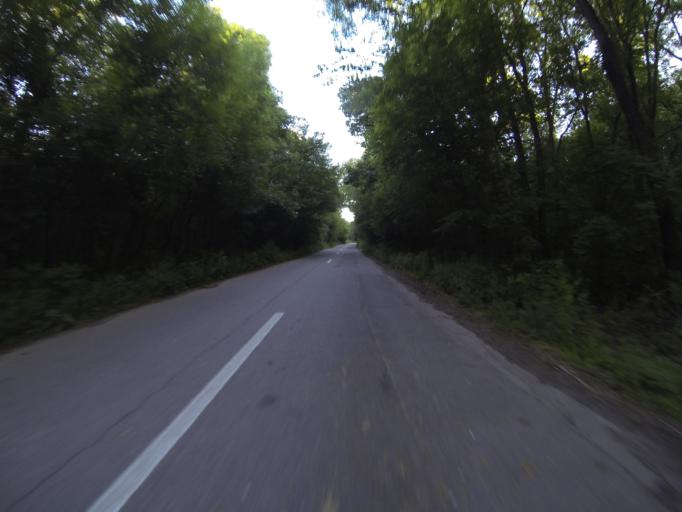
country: RO
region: Dolj
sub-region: Comuna Tuglui
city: Tuglui
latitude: 44.1648
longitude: 23.8264
